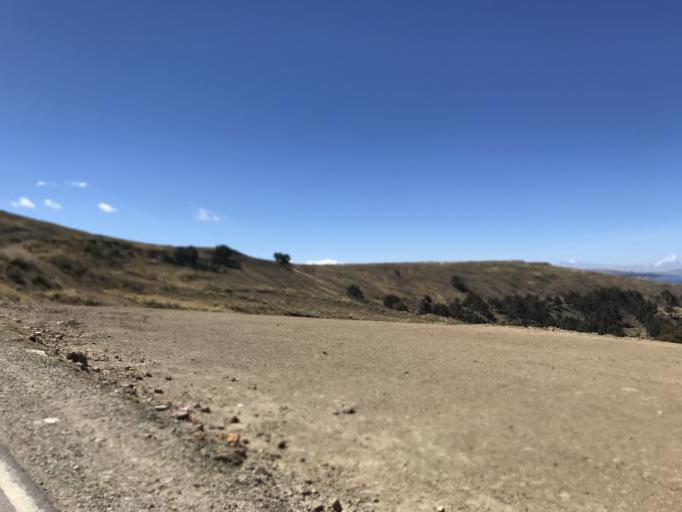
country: BO
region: La Paz
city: San Pablo
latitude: -16.2022
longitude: -68.8325
